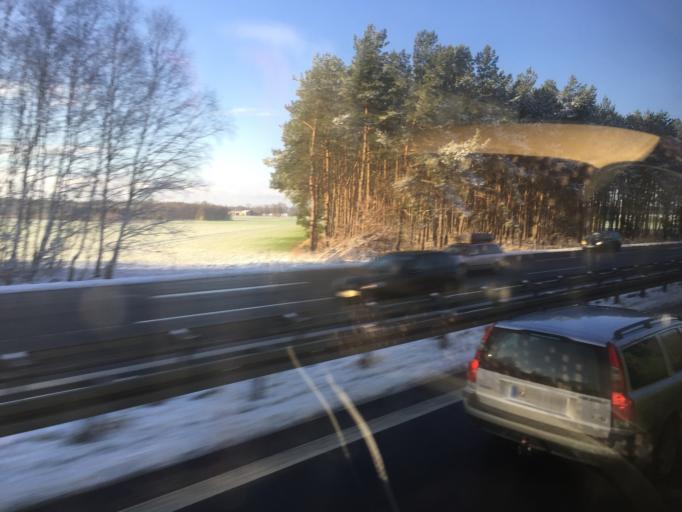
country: DE
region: Brandenburg
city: Wittstock
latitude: 53.1165
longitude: 12.4668
